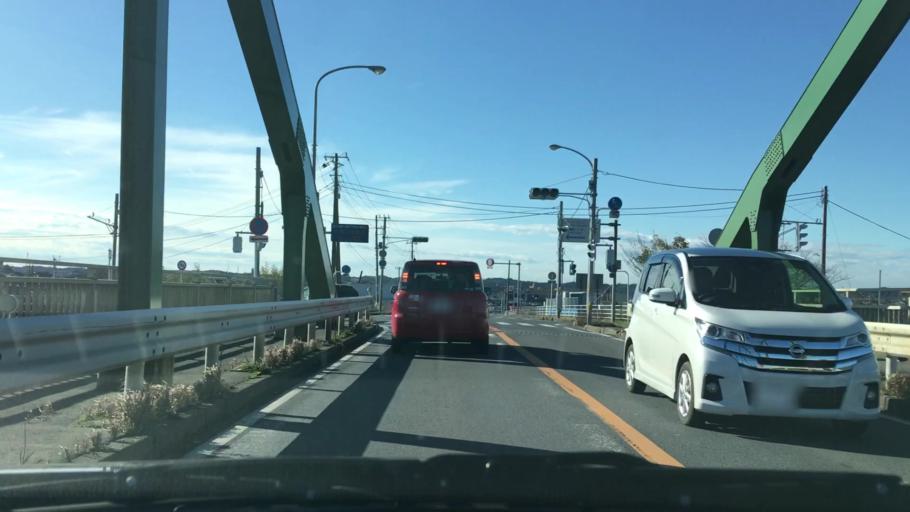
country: JP
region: Chiba
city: Omigawa
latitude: 35.8639
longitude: 140.6128
